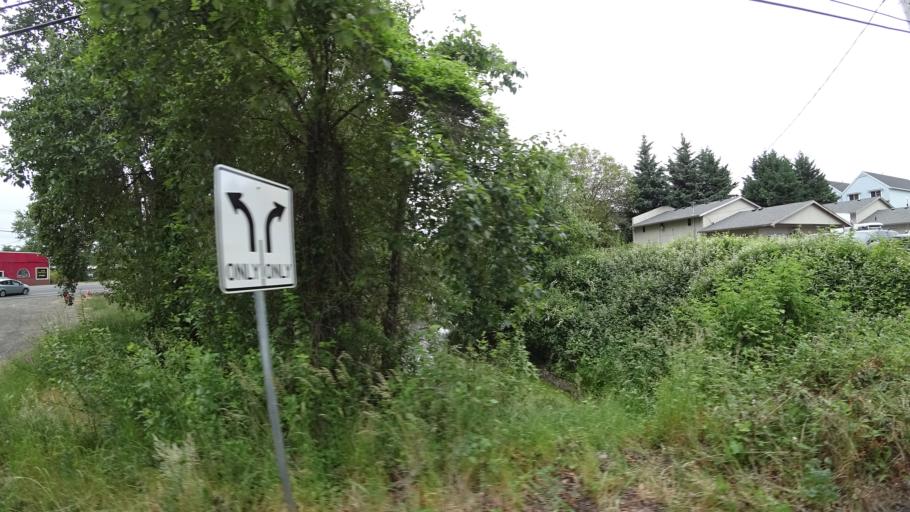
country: US
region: Washington
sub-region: Clark County
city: Vancouver
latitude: 45.6023
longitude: -122.6692
